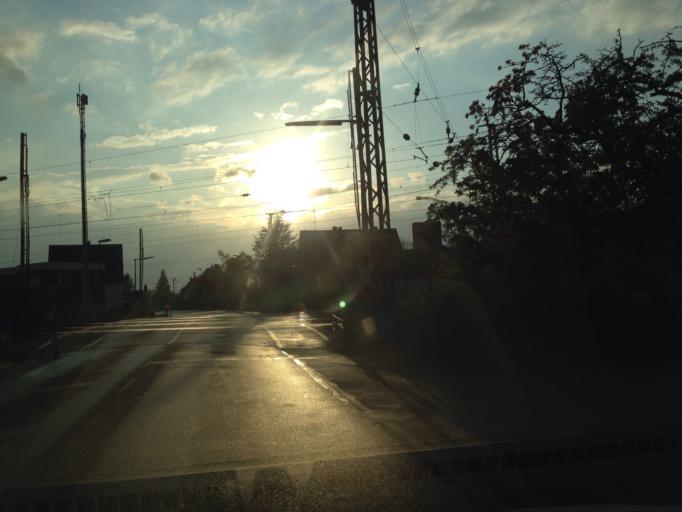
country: DE
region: North Rhine-Westphalia
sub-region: Regierungsbezirk Munster
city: Muenster
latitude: 51.9885
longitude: 7.6762
